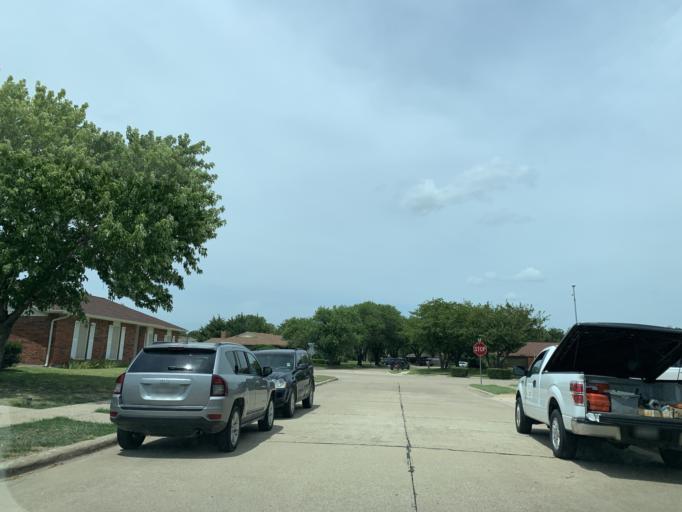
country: US
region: Texas
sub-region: Dallas County
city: Grand Prairie
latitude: 32.6579
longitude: -97.0296
